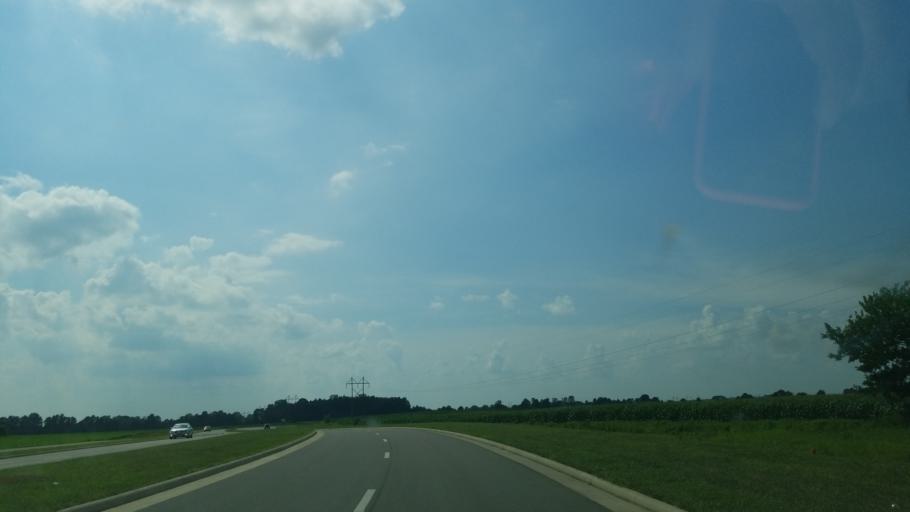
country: US
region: Ohio
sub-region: Delaware County
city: Delaware
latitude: 40.2665
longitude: -83.0936
